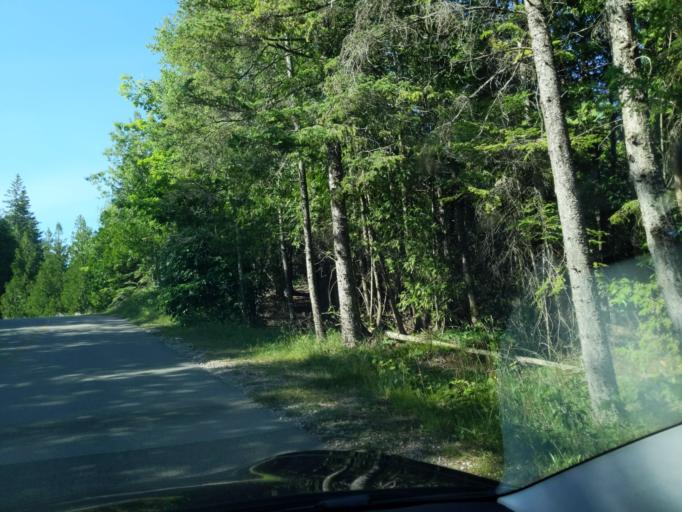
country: US
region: Michigan
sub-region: Mackinac County
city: Saint Ignace
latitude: 45.8520
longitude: -84.7187
